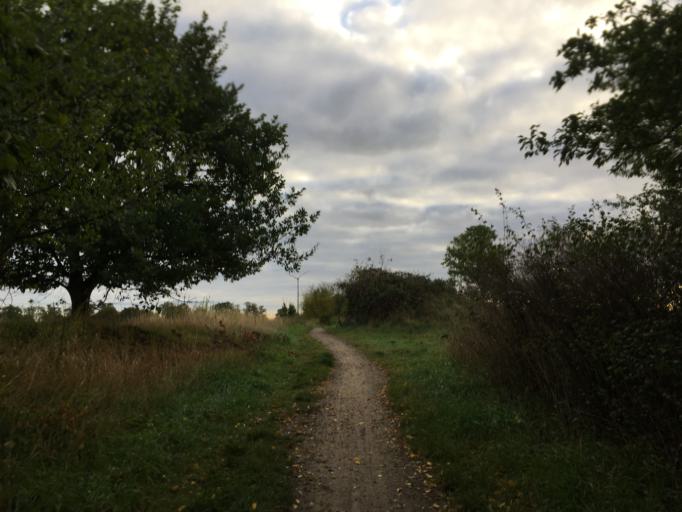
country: DE
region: Berlin
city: Stadtrandsiedlung Malchow
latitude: 52.5943
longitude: 13.4782
